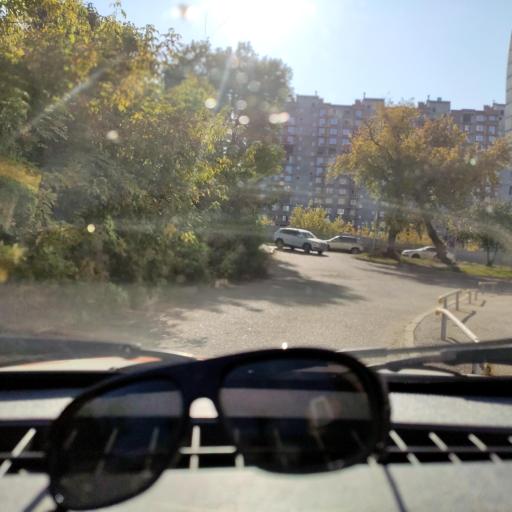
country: RU
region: Bashkortostan
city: Ufa
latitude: 54.7147
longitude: 55.9776
